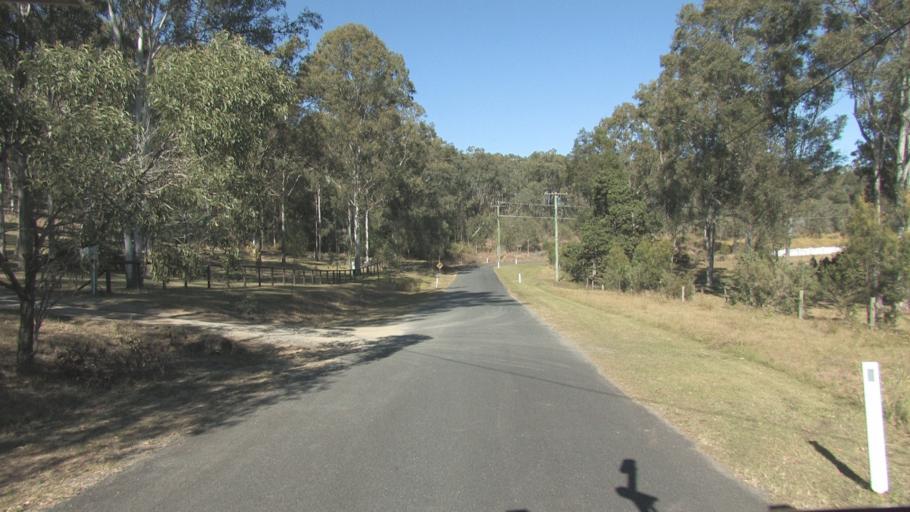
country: AU
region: Queensland
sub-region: Logan
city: Windaroo
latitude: -27.7842
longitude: 153.1476
